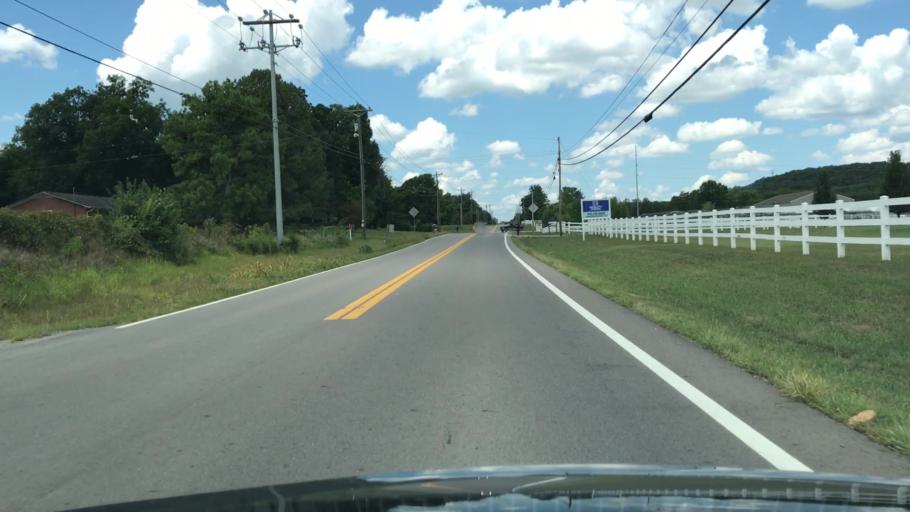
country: US
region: Tennessee
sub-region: Rutherford County
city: Smyrna
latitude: 35.8439
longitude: -86.5450
